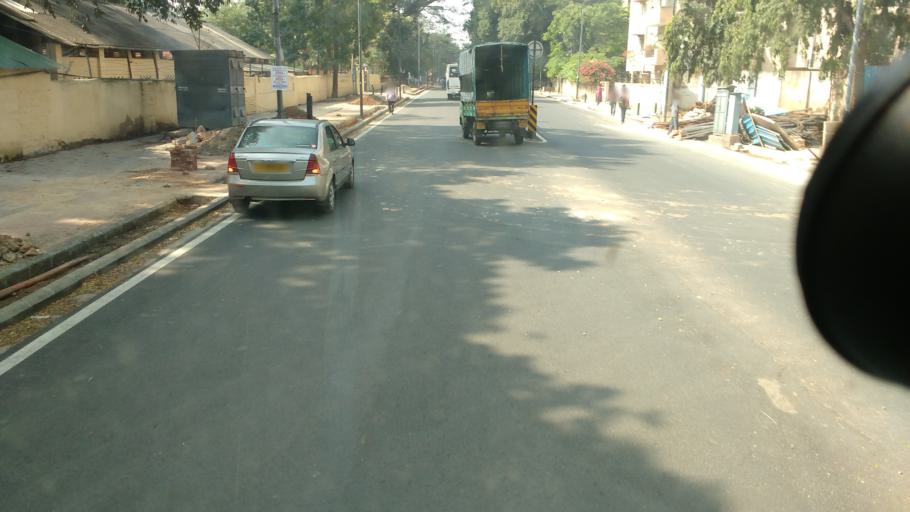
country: IN
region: Karnataka
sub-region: Bangalore Urban
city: Bangalore
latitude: 12.9706
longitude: 77.6183
